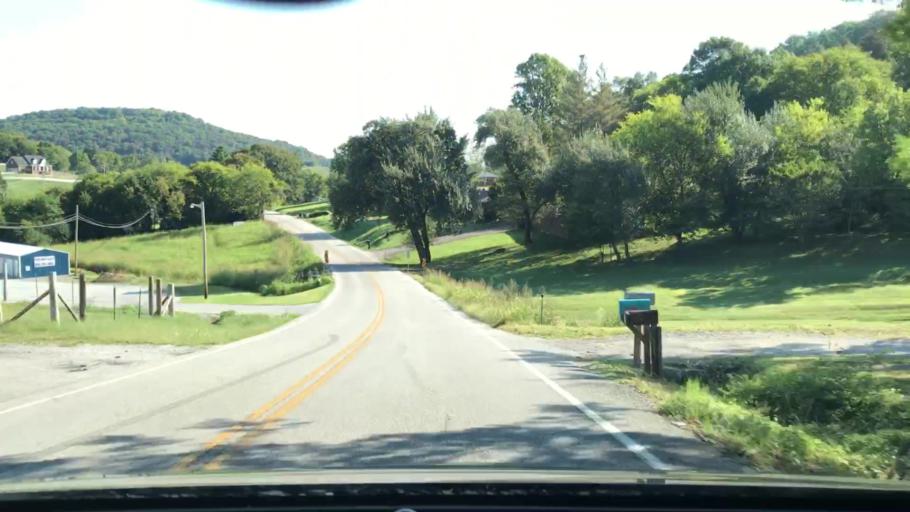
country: US
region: Tennessee
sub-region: Smith County
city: Carthage
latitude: 36.2739
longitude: -85.9541
